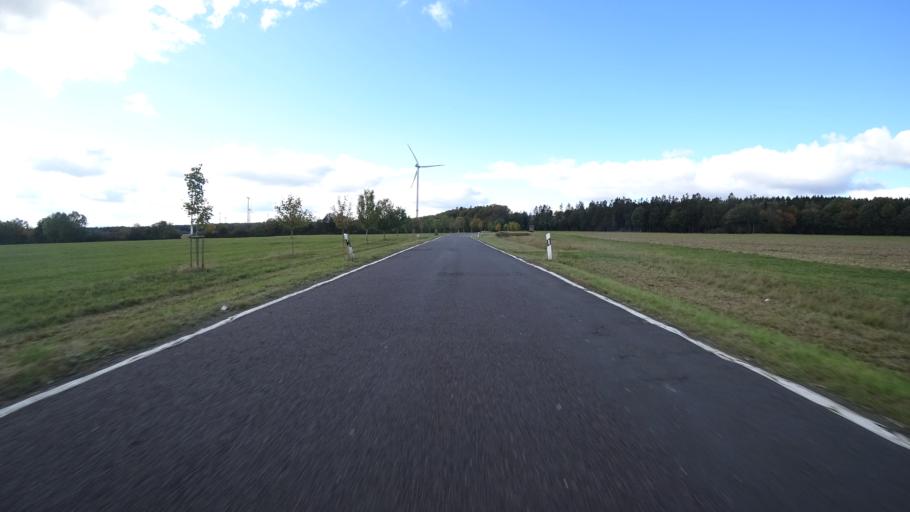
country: DE
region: Rheinland-Pfalz
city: Liebshausen
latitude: 50.0387
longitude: 7.6279
